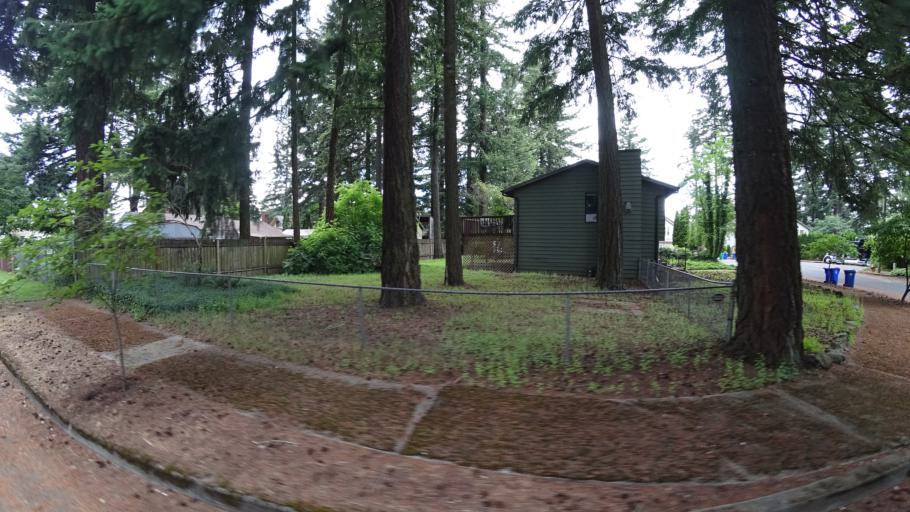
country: US
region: Oregon
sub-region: Clackamas County
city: Happy Valley
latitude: 45.5004
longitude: -122.5051
